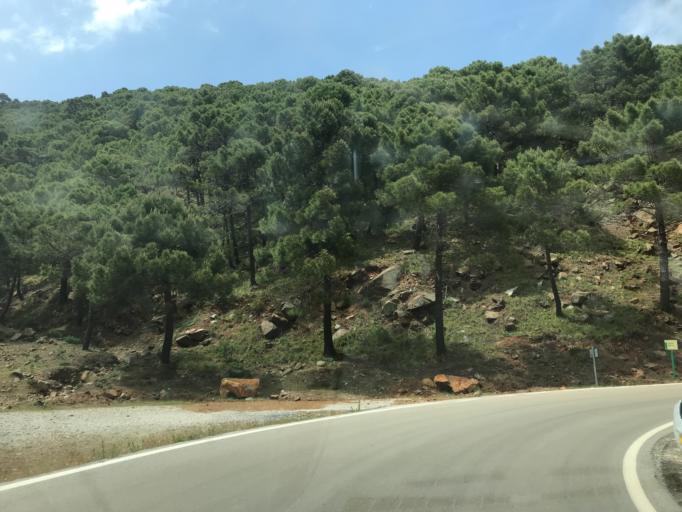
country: ES
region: Andalusia
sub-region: Provincia de Malaga
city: Estepona
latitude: 36.4897
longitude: -5.1859
